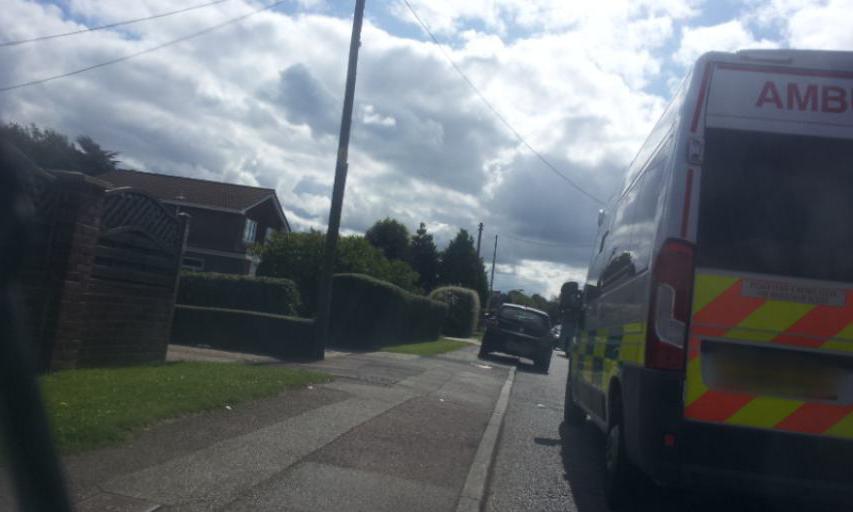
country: GB
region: England
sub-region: Kent
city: Chatham
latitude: 51.3384
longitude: 0.5207
